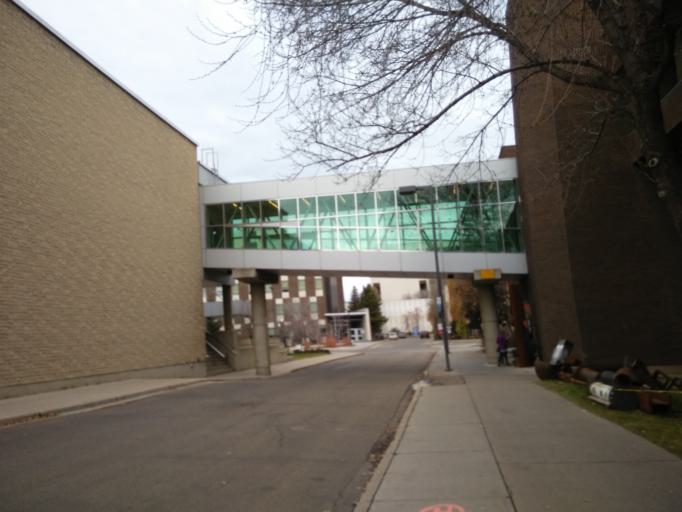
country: CA
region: Alberta
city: Edmonton
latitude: 53.5239
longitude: -113.5198
